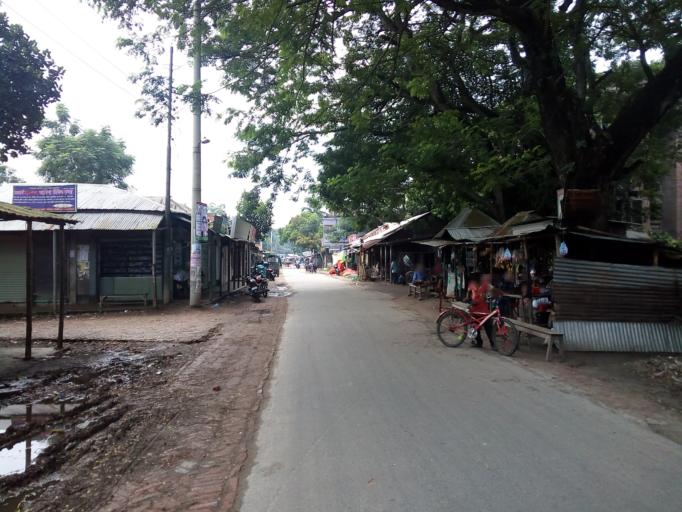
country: BD
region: Dhaka
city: Faridpur
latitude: 23.5445
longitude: 89.6302
